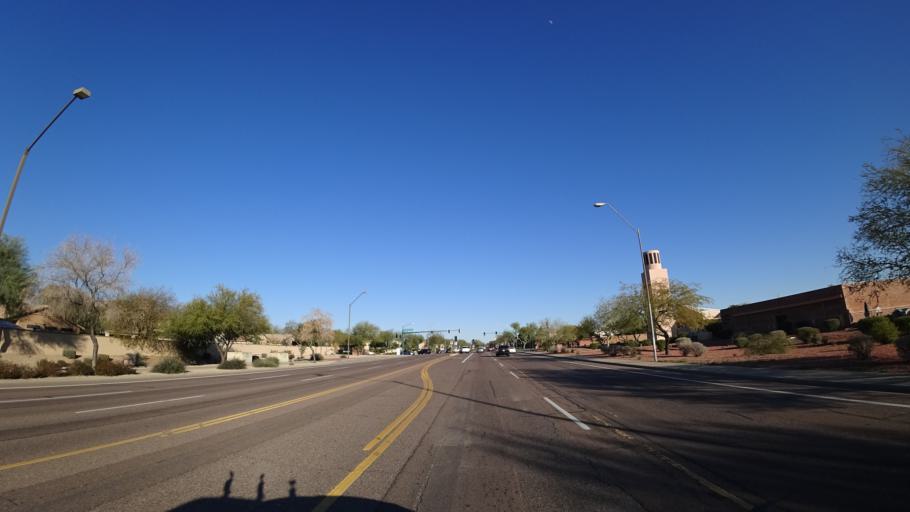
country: US
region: Arizona
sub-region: Maricopa County
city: Anthem
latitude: 33.7128
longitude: -112.1451
